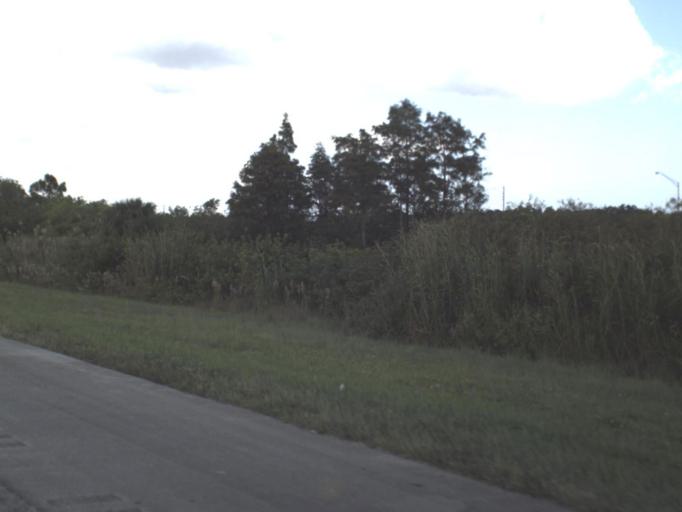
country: US
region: Florida
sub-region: Martin County
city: Hobe Sound
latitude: 27.0076
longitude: -80.2109
